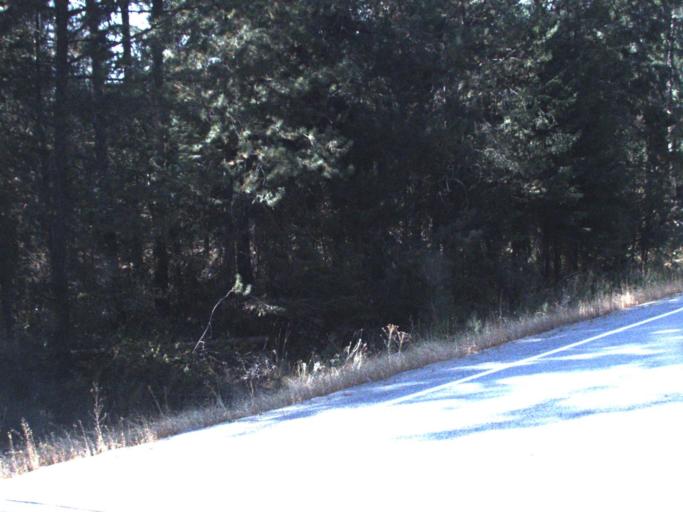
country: US
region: Washington
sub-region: Pend Oreille County
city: Newport
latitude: 48.1226
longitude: -117.2732
